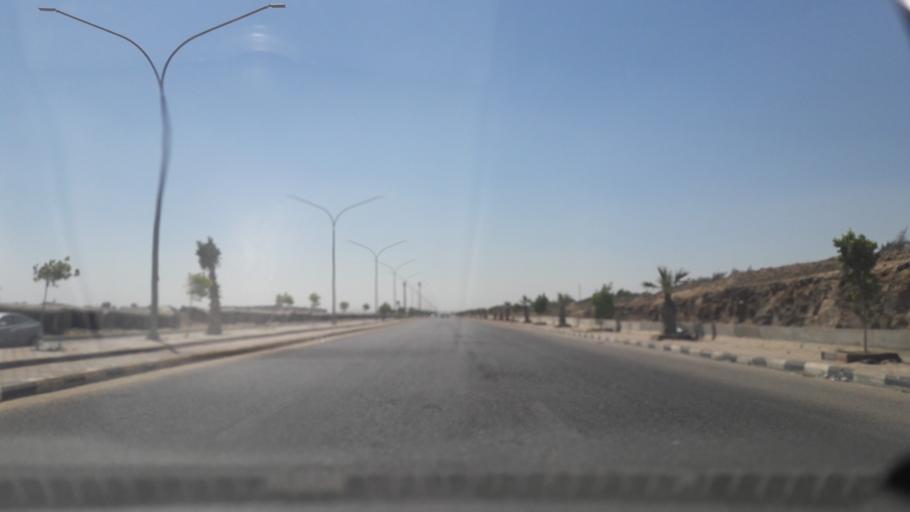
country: EG
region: Al Jizah
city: Madinat Sittah Uktubar
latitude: 29.9548
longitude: 31.0142
